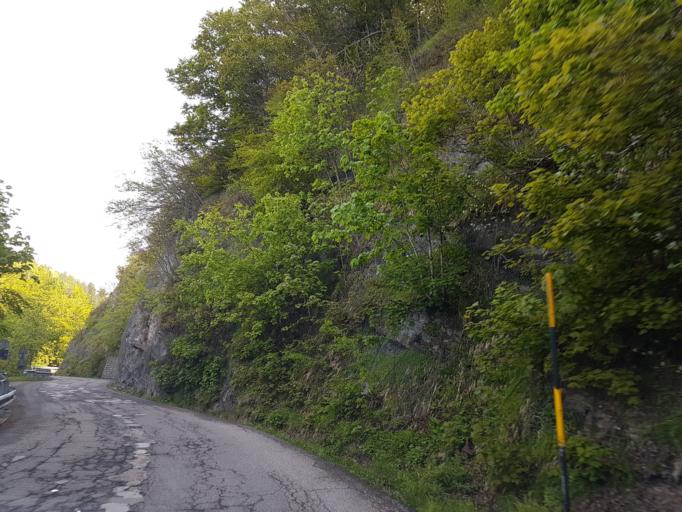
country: IT
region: Emilia-Romagna
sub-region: Forli-Cesena
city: San Piero in Bagno
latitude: 43.7987
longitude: 11.9142
